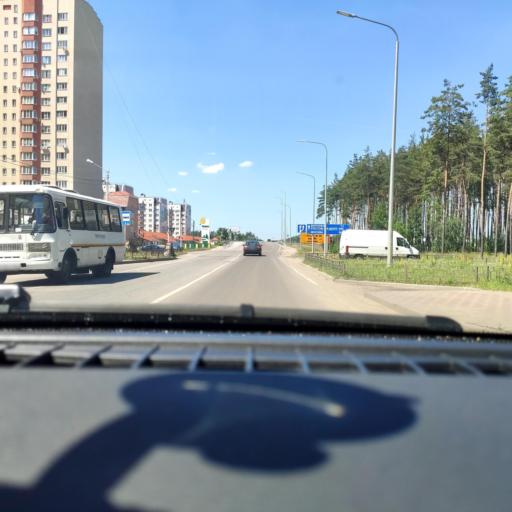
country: RU
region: Voronezj
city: Somovo
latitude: 51.7431
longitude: 39.3153
